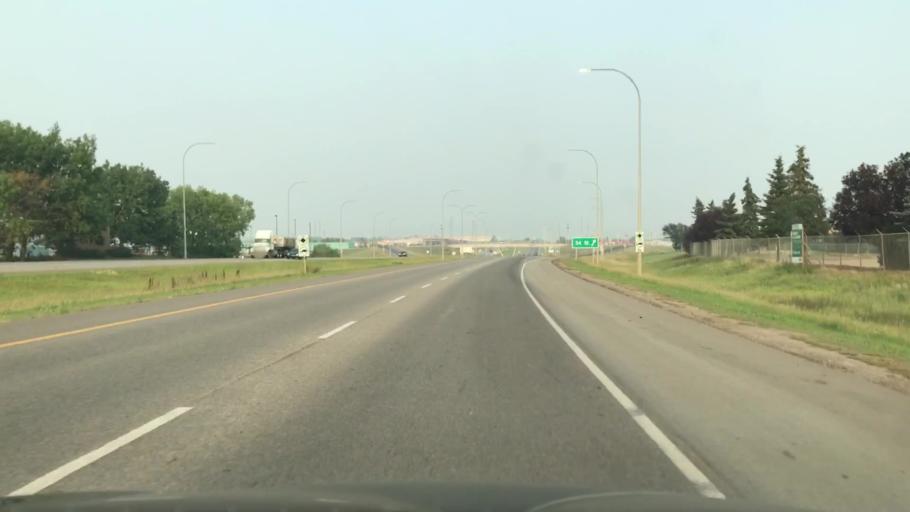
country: CA
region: Alberta
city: Edmonton
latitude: 53.5166
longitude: -113.4021
